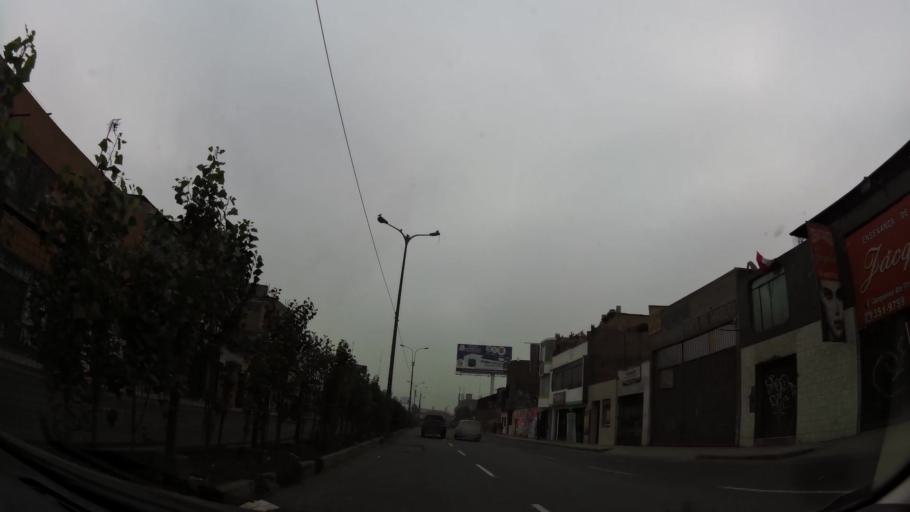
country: PE
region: Lima
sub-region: Lima
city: Vitarte
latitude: -12.0249
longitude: -76.9168
